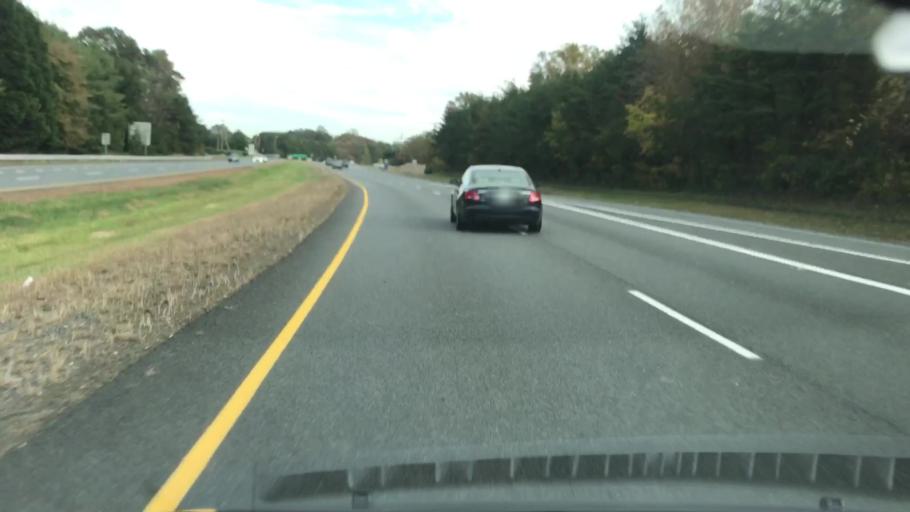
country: US
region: Virginia
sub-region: Fairfax County
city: Fairfax Station
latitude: 38.7870
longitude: -77.3226
